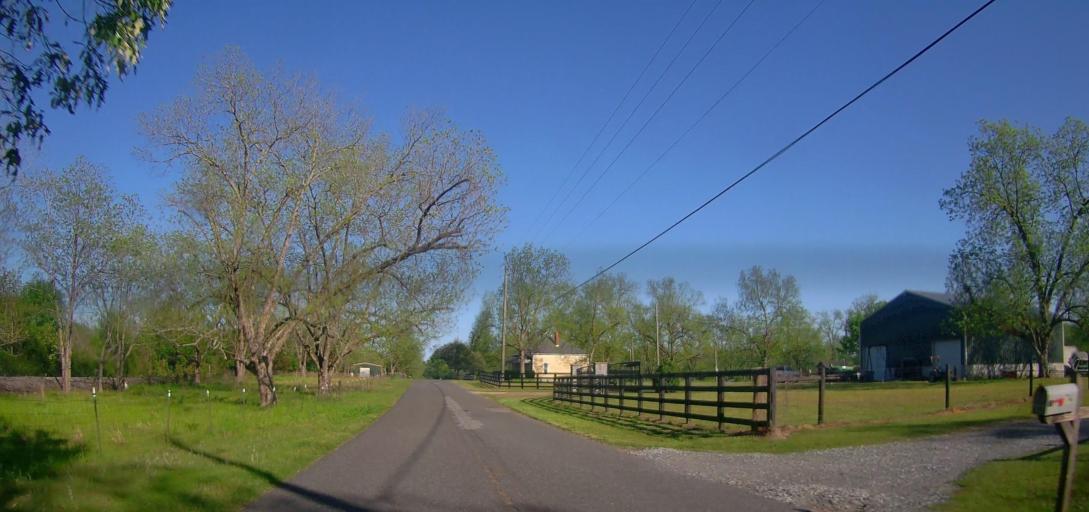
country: US
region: Georgia
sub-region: Houston County
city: Perry
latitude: 32.4820
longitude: -83.8011
